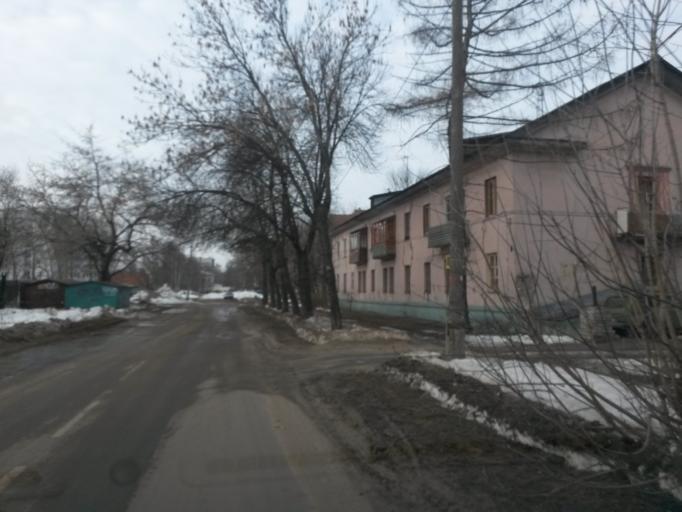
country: RU
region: Jaroslavl
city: Yaroslavl
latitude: 57.6336
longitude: 39.8405
